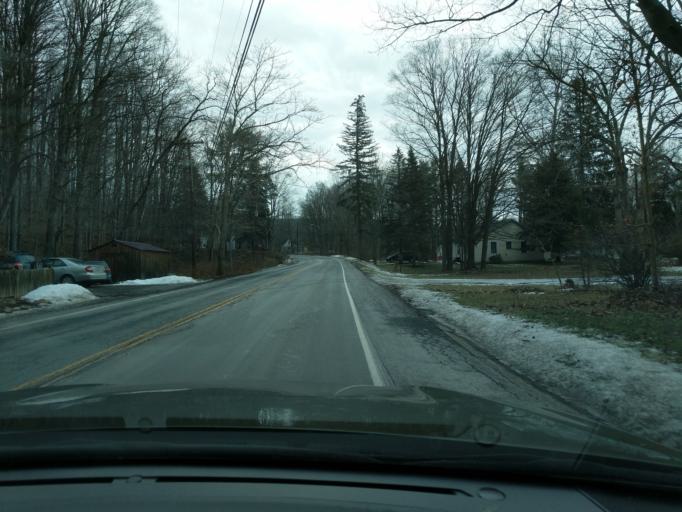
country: US
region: New York
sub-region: Tompkins County
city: East Ithaca
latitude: 42.3869
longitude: -76.4059
